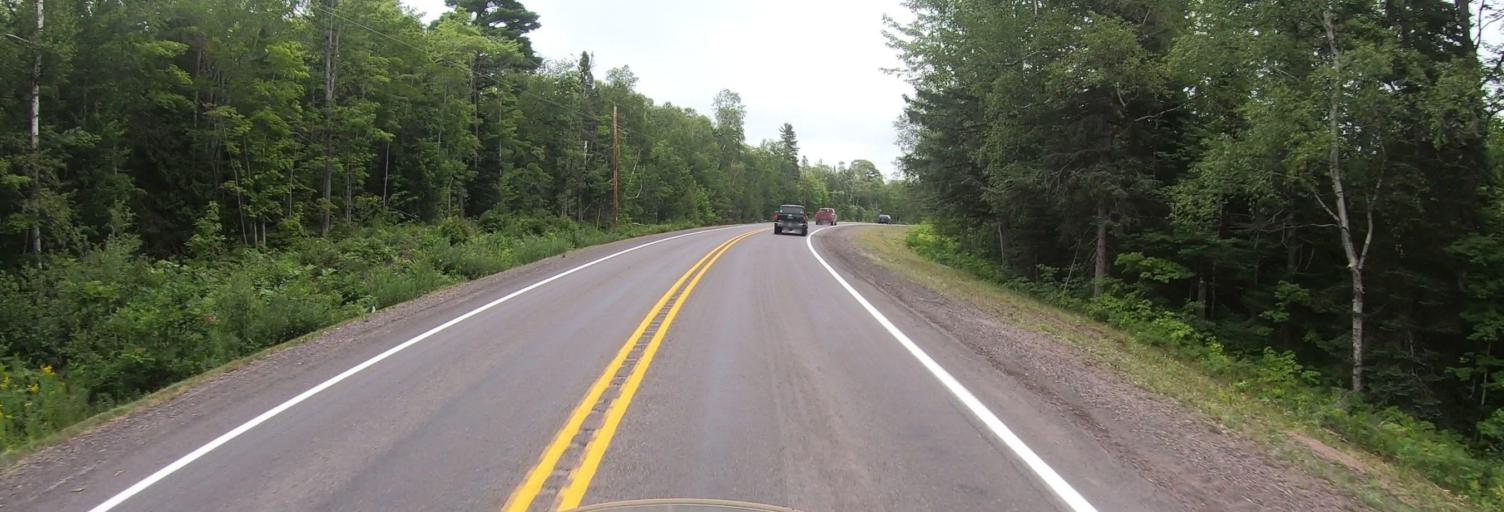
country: US
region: Michigan
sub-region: Keweenaw County
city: Eagle River
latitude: 47.4191
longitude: -88.1309
